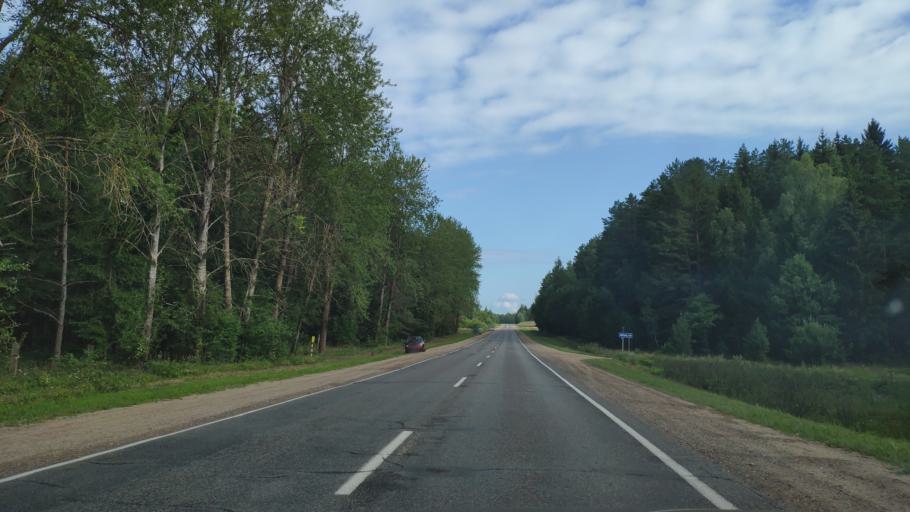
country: BY
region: Minsk
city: Zaslawye
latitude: 53.9567
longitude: 27.2454
